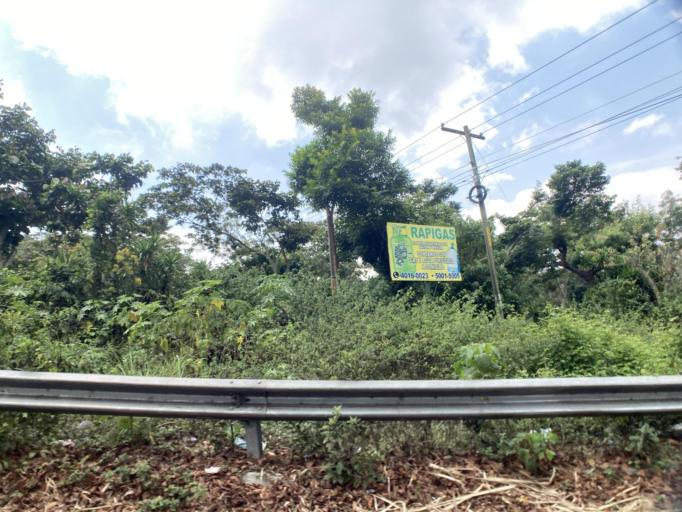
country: GT
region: Guatemala
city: Villa Canales
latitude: 14.4160
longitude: -90.5310
